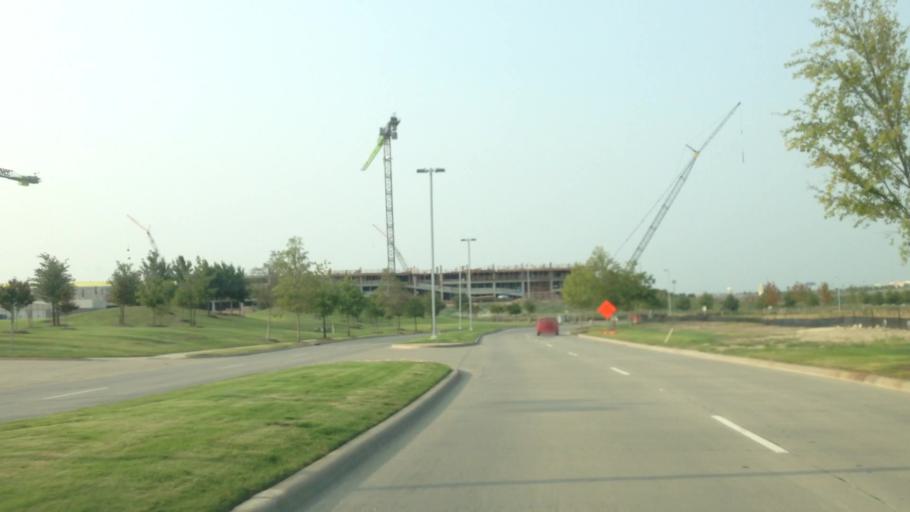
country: US
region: Texas
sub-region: Denton County
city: The Colony
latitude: 33.0694
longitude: -96.8601
